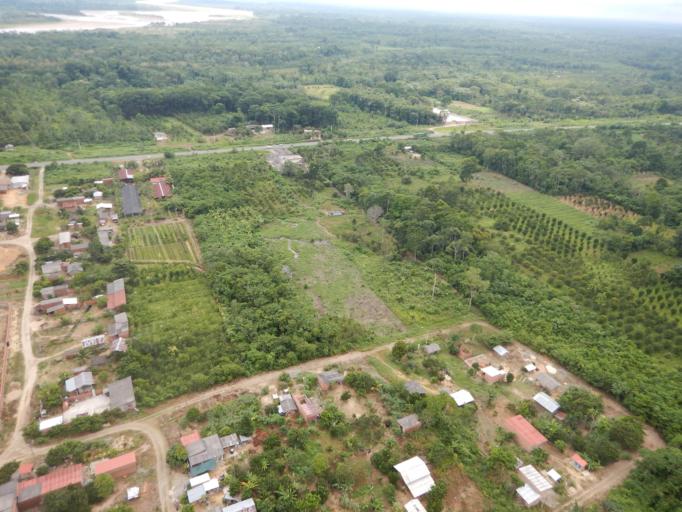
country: BO
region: Cochabamba
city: Chimore
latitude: -16.9966
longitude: -65.0941
